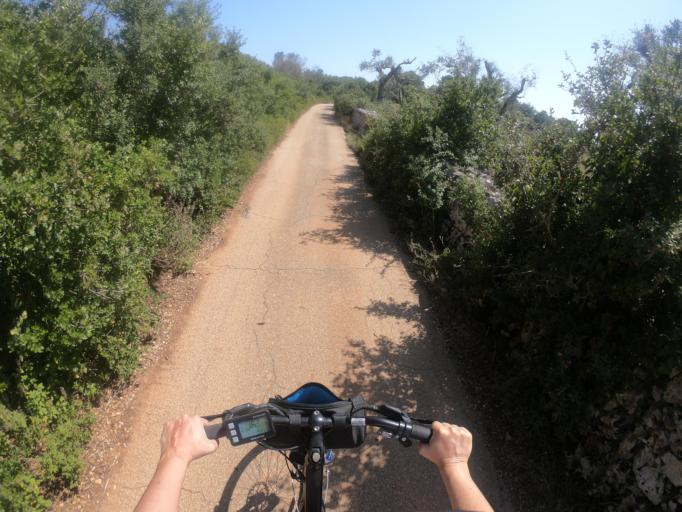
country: IT
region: Apulia
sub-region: Provincia di Lecce
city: Specchia
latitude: 39.9328
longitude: 18.2763
